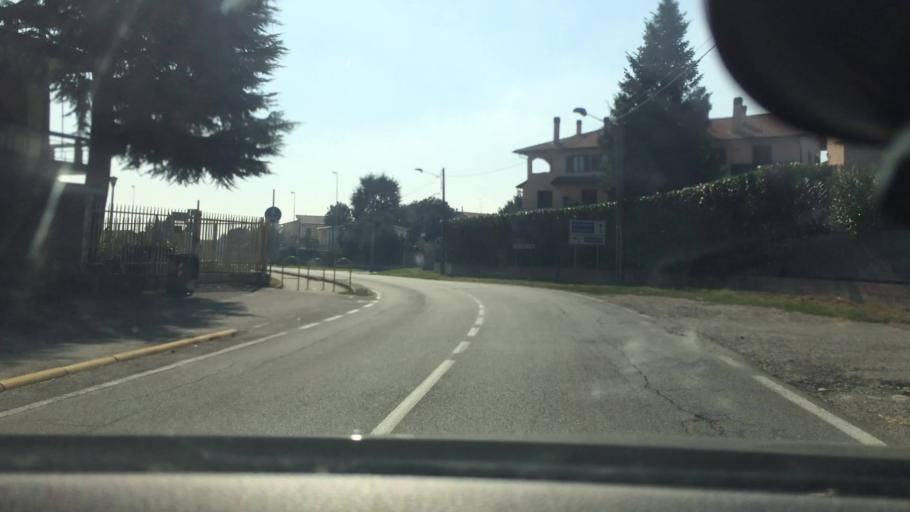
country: IT
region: Lombardy
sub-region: Citta metropolitana di Milano
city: Busto Garolfo
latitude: 45.5392
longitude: 8.8753
